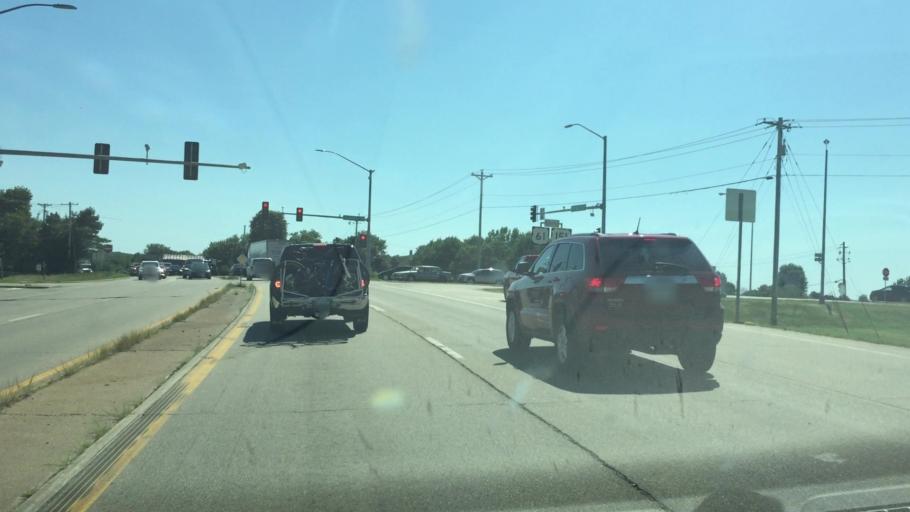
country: US
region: Iowa
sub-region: Dubuque County
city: Dubuque
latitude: 42.4551
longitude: -90.6775
